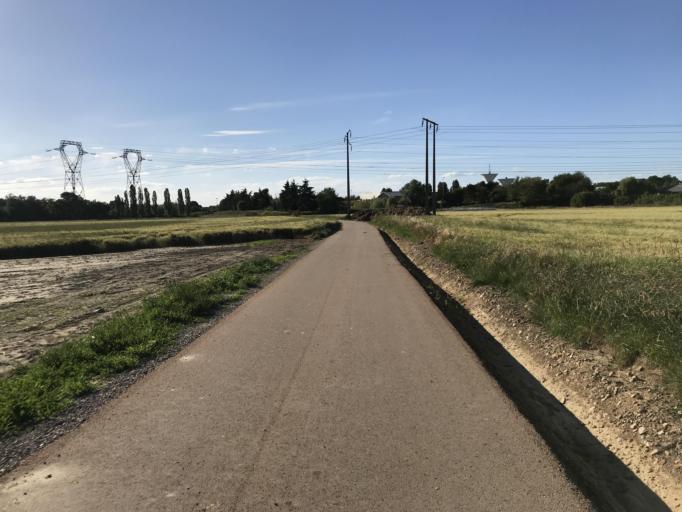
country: FR
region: Ile-de-France
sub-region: Departement de l'Essonne
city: Villejust
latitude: 48.6773
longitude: 2.2141
